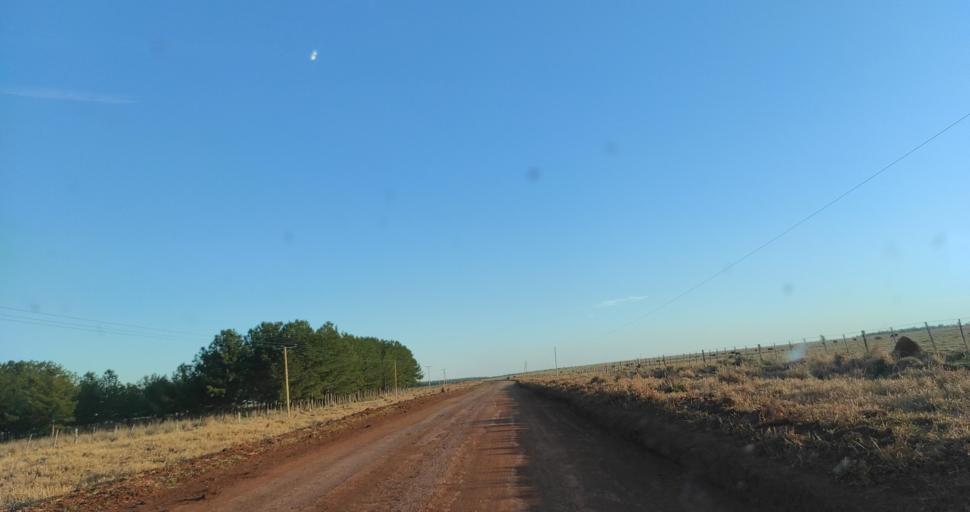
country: PY
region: Itapua
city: San Juan del Parana
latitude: -27.4311
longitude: -56.0841
